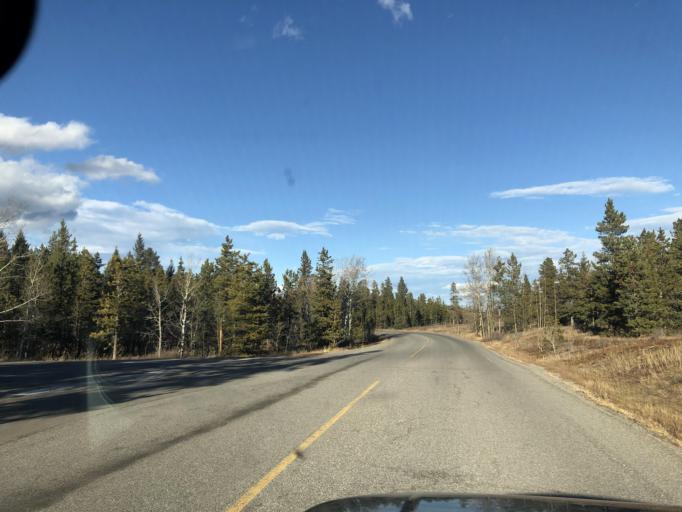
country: CA
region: Alberta
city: Canmore
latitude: 51.0794
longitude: -115.0636
